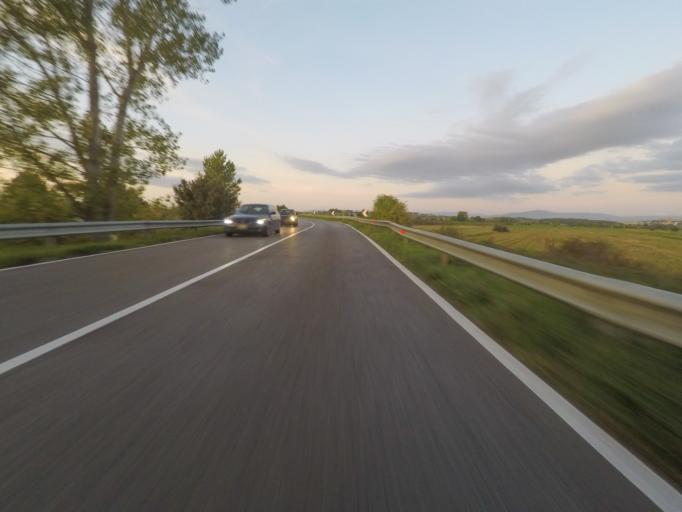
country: IT
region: Tuscany
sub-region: Provincia di Siena
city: Sinalunga
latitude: 43.1953
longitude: 11.7611
